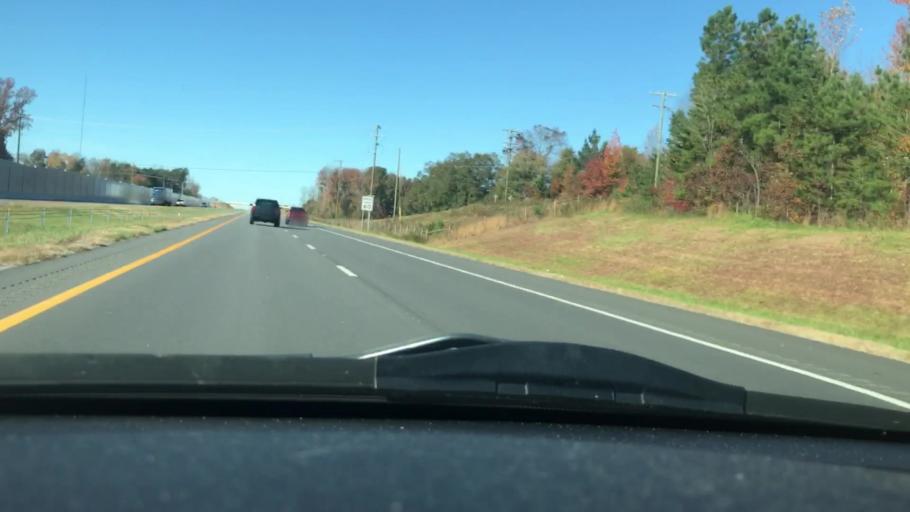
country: US
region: North Carolina
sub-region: Guilford County
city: Summerfield
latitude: 36.2582
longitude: -79.9248
